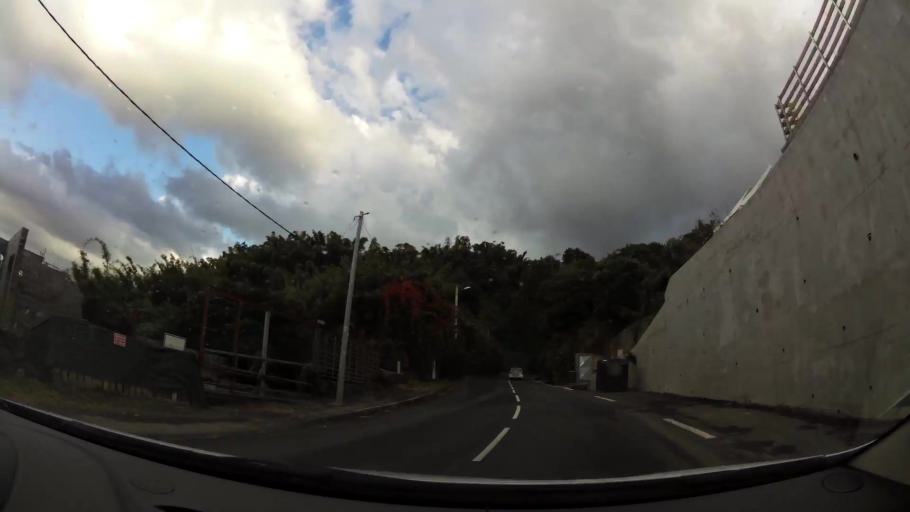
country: RE
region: Reunion
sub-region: Reunion
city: Saint-Denis
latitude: -20.9053
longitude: 55.4419
